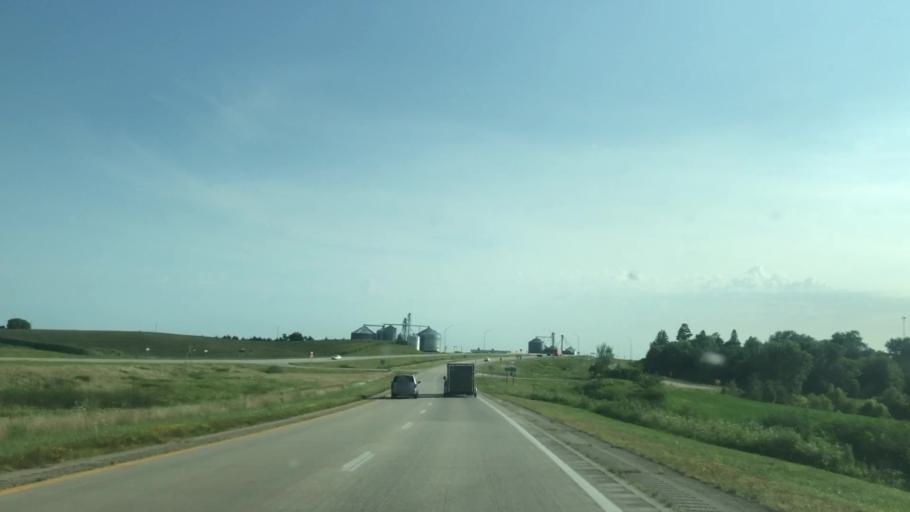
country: US
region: Iowa
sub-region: Marshall County
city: Marshalltown
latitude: 42.0131
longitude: -93.0163
